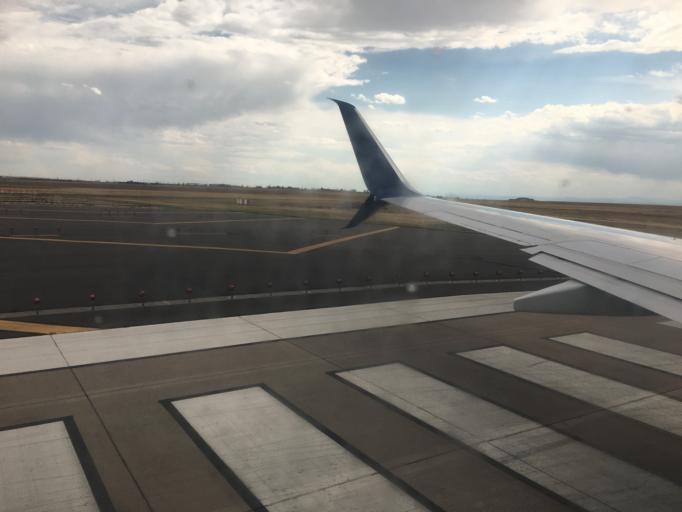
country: US
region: Colorado
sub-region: Weld County
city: Lochbuie
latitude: 39.8520
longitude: -104.6963
